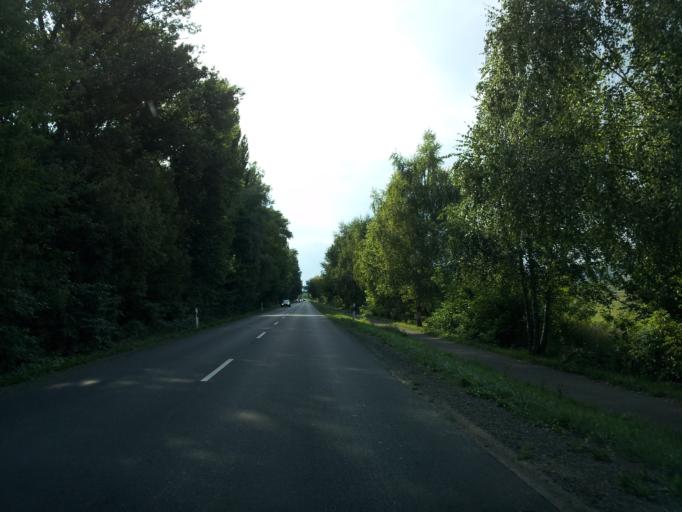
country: HU
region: Pest
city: Veroce
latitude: 47.8172
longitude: 19.0624
